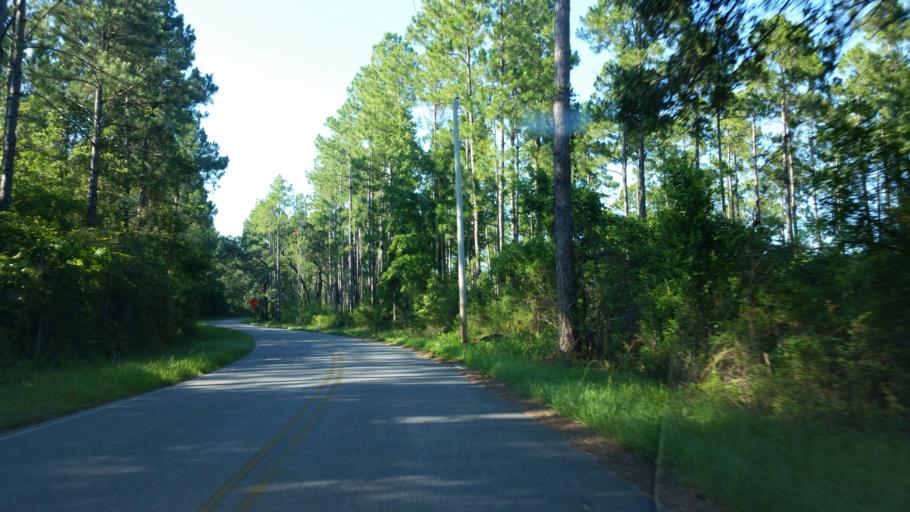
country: US
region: Florida
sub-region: Escambia County
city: Bellview
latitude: 30.4861
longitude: -87.3878
